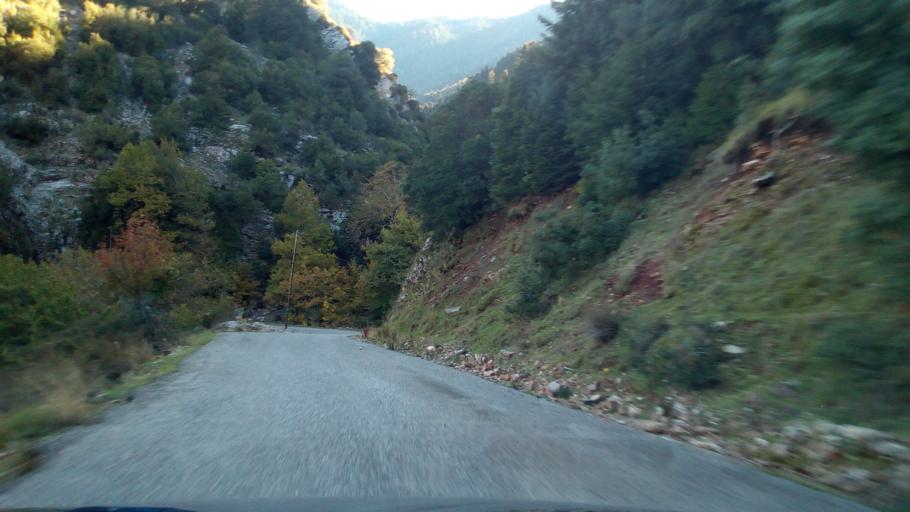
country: GR
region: West Greece
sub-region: Nomos Aitolias kai Akarnanias
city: Nafpaktos
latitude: 38.5546
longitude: 21.8576
